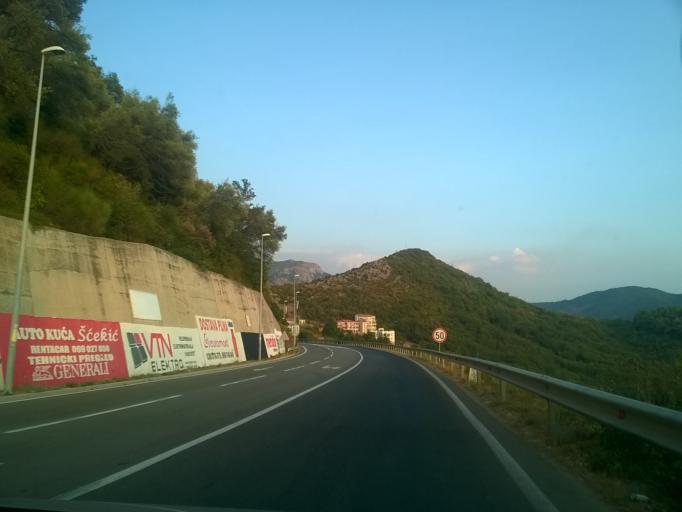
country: ME
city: Petrovac na Moru
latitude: 42.2042
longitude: 18.9513
